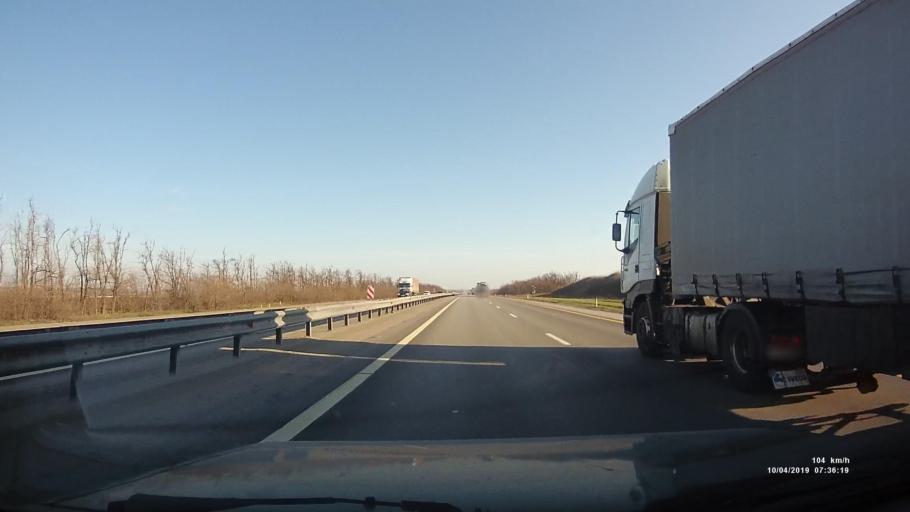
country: RU
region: Rostov
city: Likhoy
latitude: 48.0555
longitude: 40.2595
